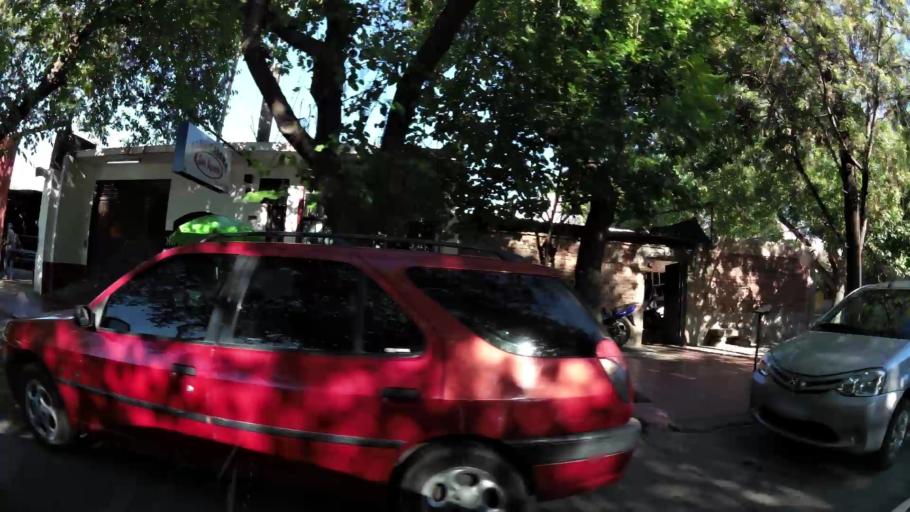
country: AR
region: Mendoza
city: Las Heras
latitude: -32.8714
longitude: -68.8260
